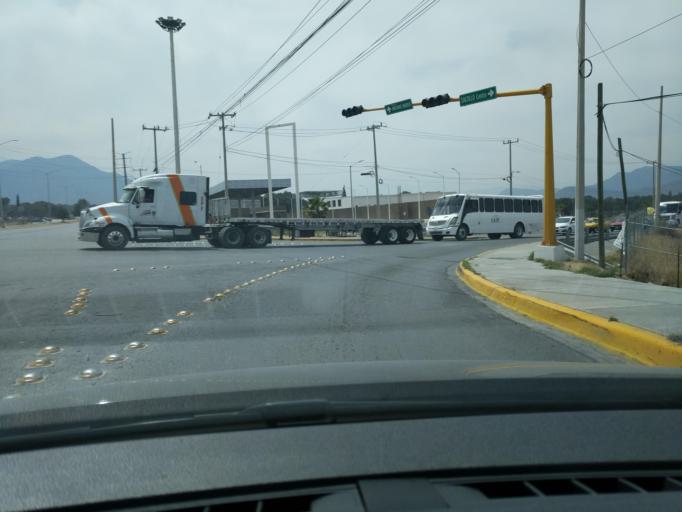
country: MX
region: Coahuila
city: Saltillo
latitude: 25.3531
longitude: -101.0224
